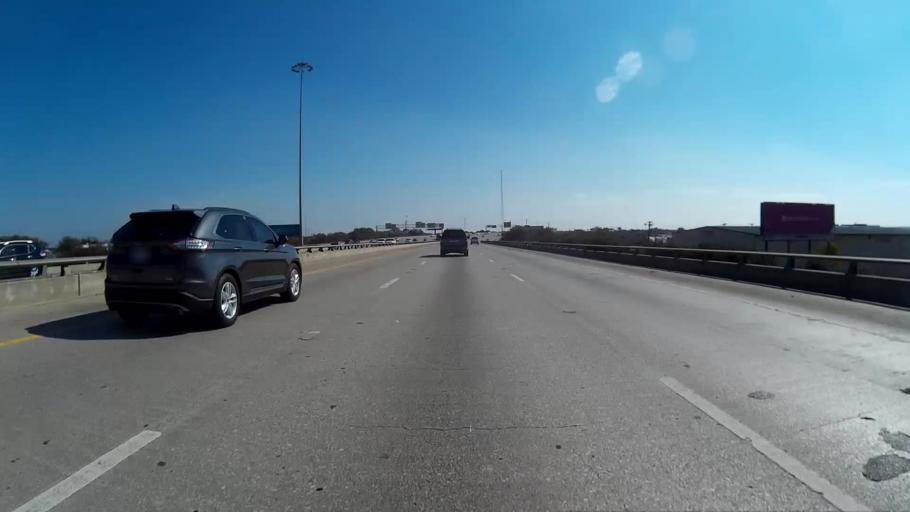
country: US
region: Texas
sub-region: Dallas County
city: Dallas
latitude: 32.7770
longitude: -96.7806
